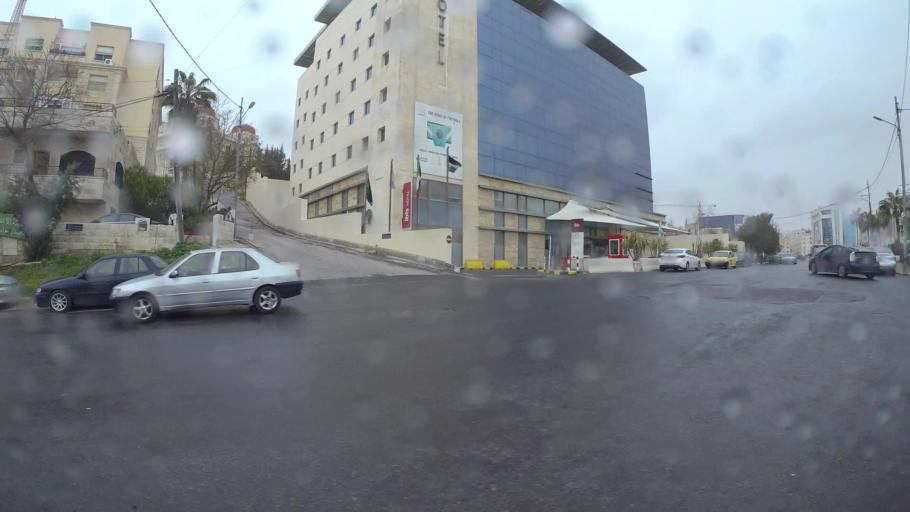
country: JO
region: Amman
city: Al Jubayhah
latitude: 31.9898
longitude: 35.8652
